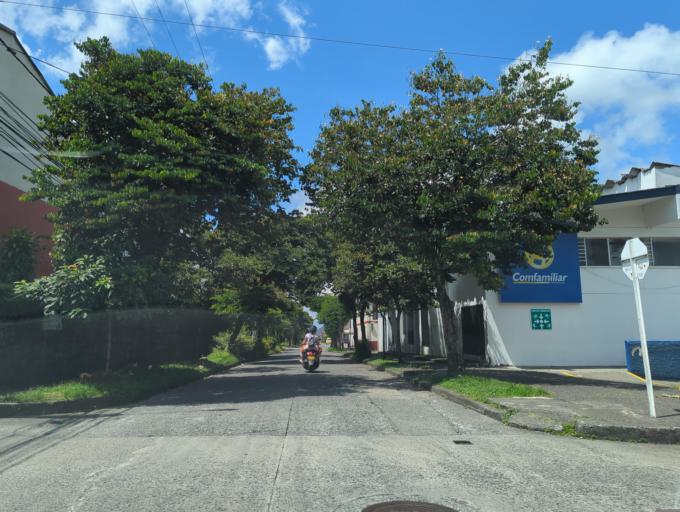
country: CO
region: Risaralda
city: Pereira
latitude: 4.8183
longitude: -75.7031
